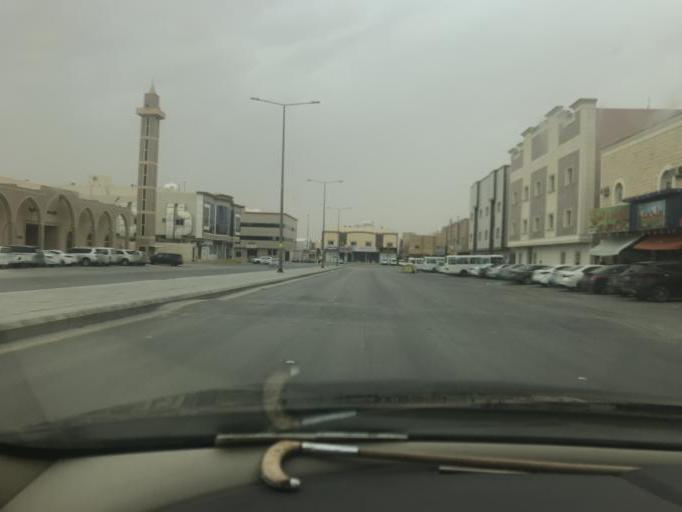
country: SA
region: Ar Riyad
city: Riyadh
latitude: 24.7894
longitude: 46.6926
